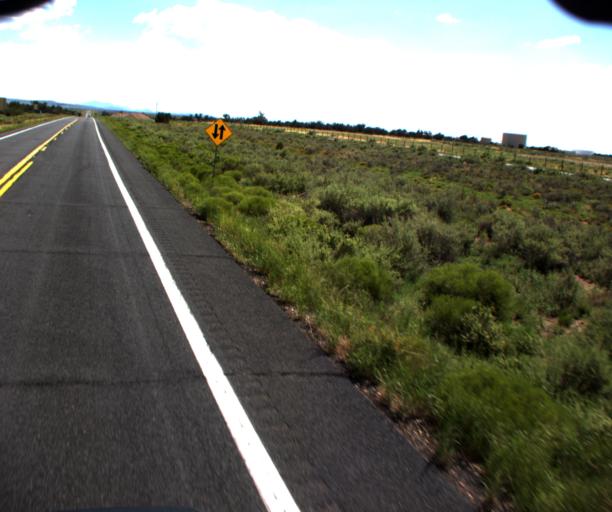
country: US
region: Arizona
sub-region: Coconino County
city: Grand Canyon Village
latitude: 35.6469
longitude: -112.1402
